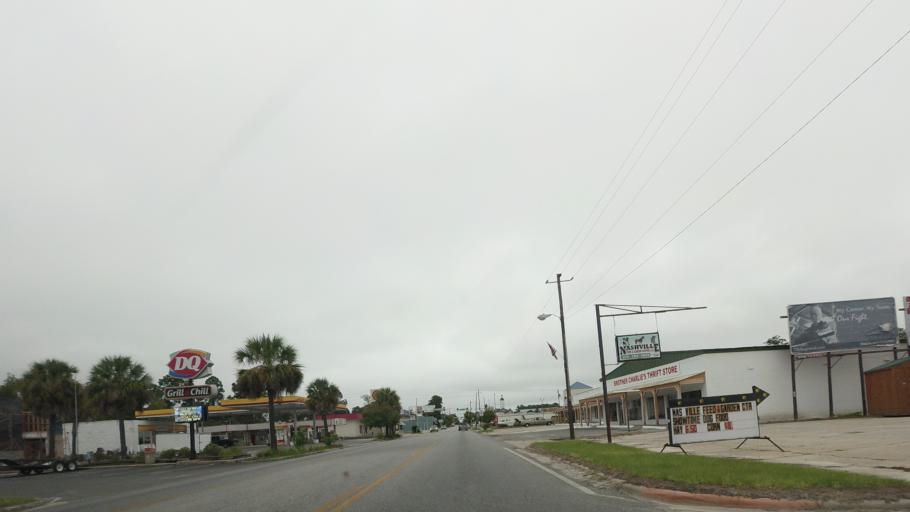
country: US
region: Georgia
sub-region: Berrien County
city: Nashville
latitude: 31.2021
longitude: -83.2508
